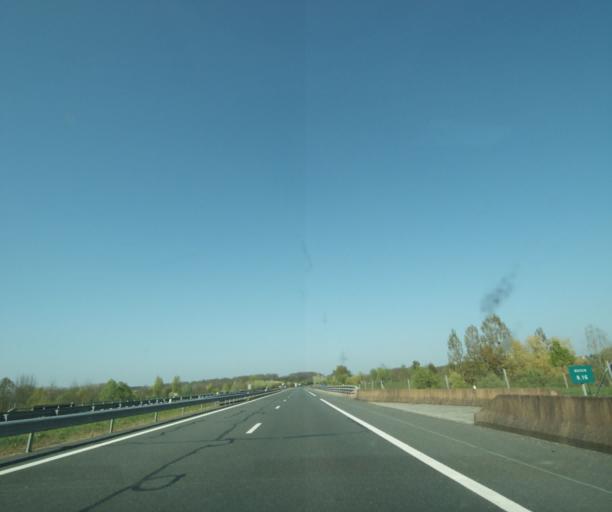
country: FR
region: Centre
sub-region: Departement du Loiret
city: Dordives
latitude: 48.1560
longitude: 2.7542
